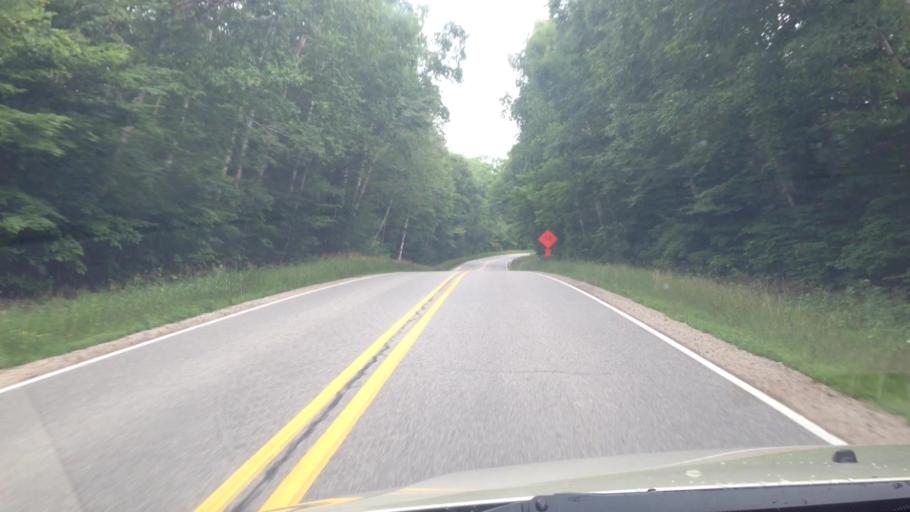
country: US
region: Michigan
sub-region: Mackinac County
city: Saint Ignace
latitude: 46.0433
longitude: -85.1130
